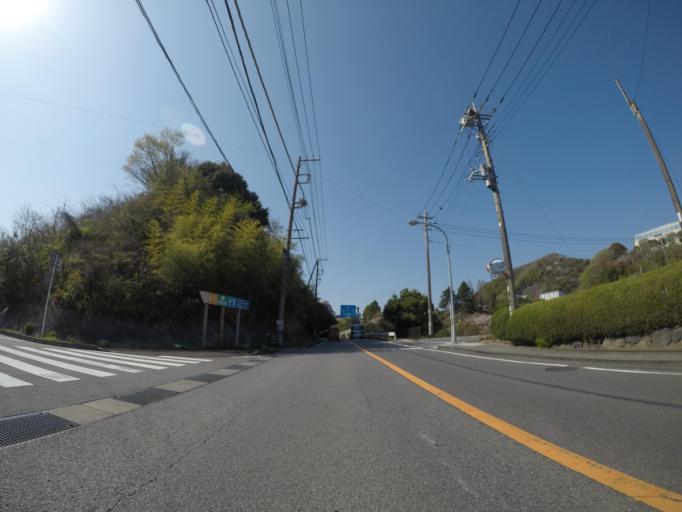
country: JP
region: Shizuoka
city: Mishima
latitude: 35.0400
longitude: 138.9240
